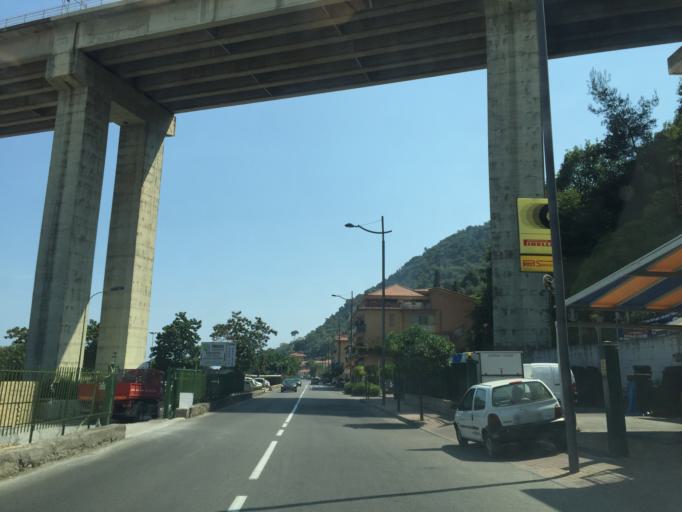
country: IT
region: Liguria
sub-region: Provincia di Imperia
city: Camporosso
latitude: 43.8025
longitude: 7.6249
